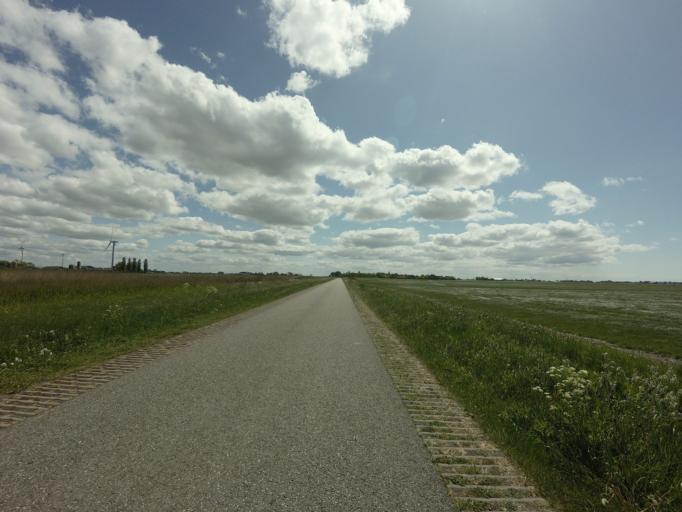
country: NL
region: Friesland
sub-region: Sudwest Fryslan
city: Makkum
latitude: 53.0911
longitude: 5.4150
